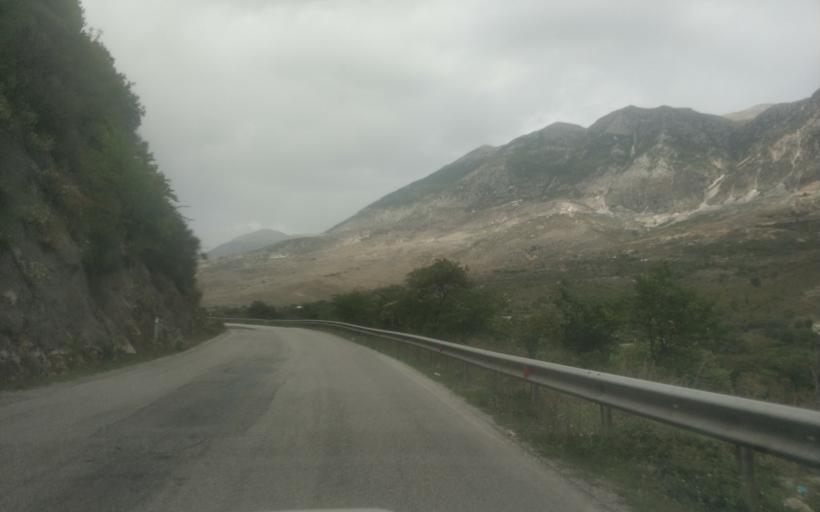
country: AL
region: Gjirokaster
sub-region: Rrethi i Gjirokastres
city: Picar
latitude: 40.2278
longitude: 20.0851
